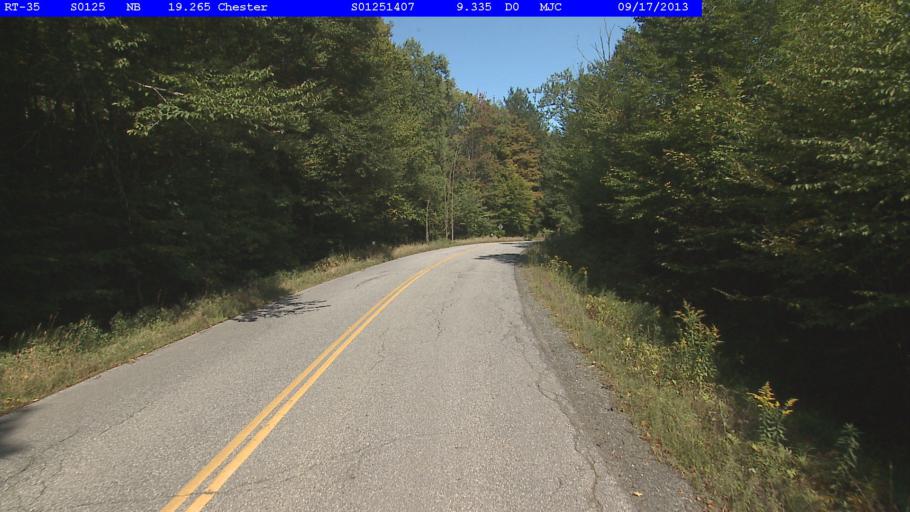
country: US
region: Vermont
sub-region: Windsor County
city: Chester
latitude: 43.2398
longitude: -72.6101
